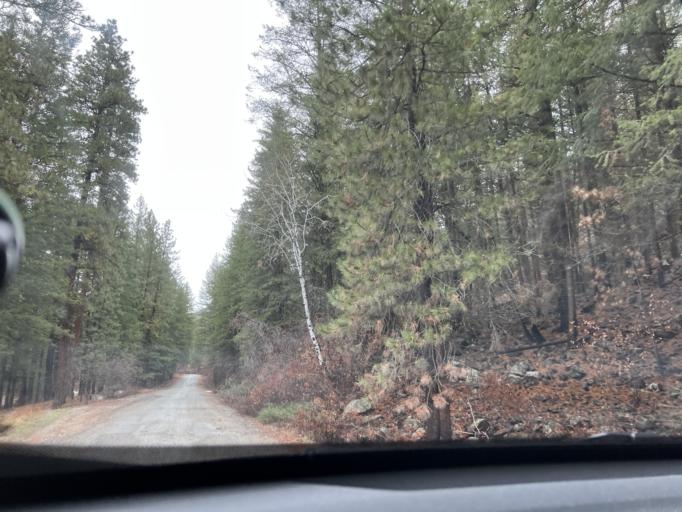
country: US
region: Washington
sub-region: Okanogan County
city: Brewster
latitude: 48.5700
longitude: -120.1711
